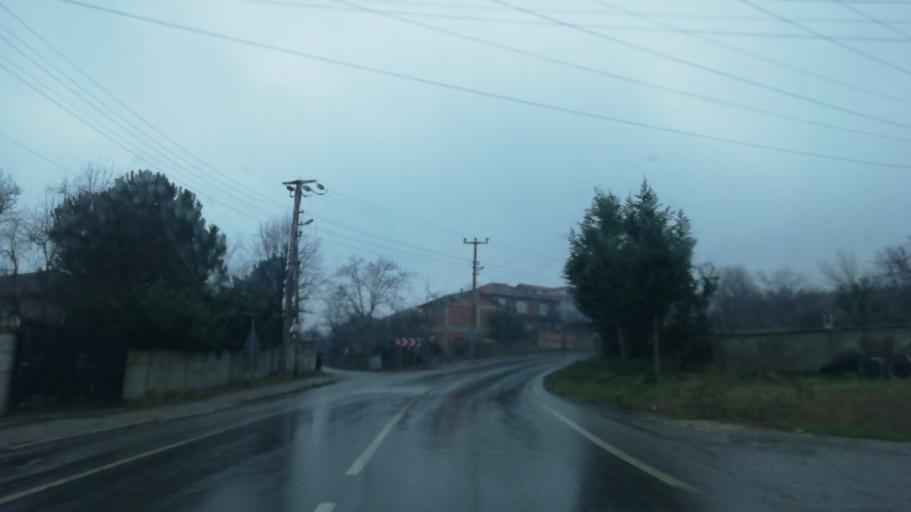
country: TR
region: Sakarya
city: Karapurcek
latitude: 40.6884
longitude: 30.5097
